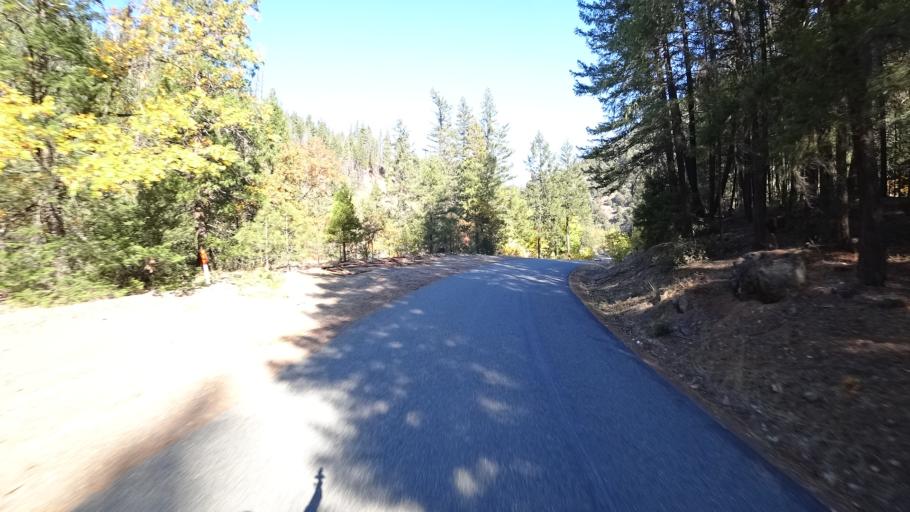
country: US
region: California
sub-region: Siskiyou County
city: Happy Camp
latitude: 41.6473
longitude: -123.1144
